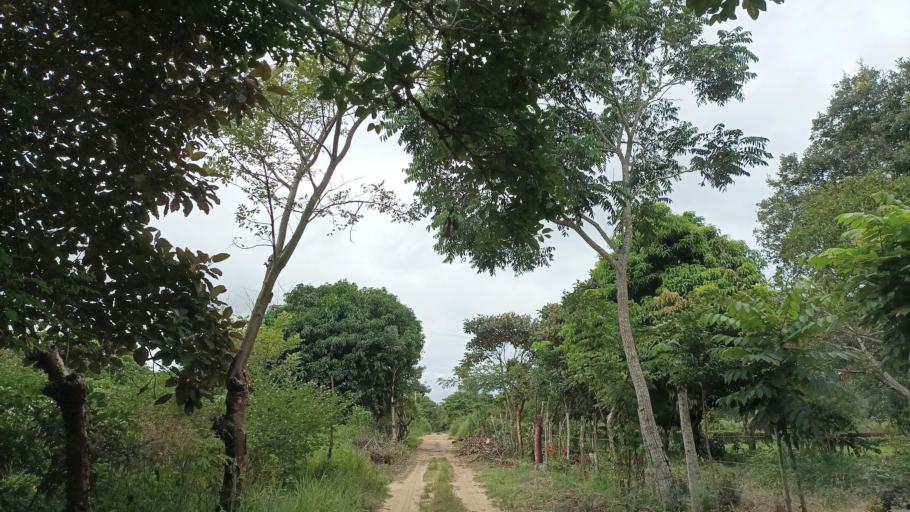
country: MX
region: Veracruz
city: Minatitlan
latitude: 18.0403
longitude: -94.5616
